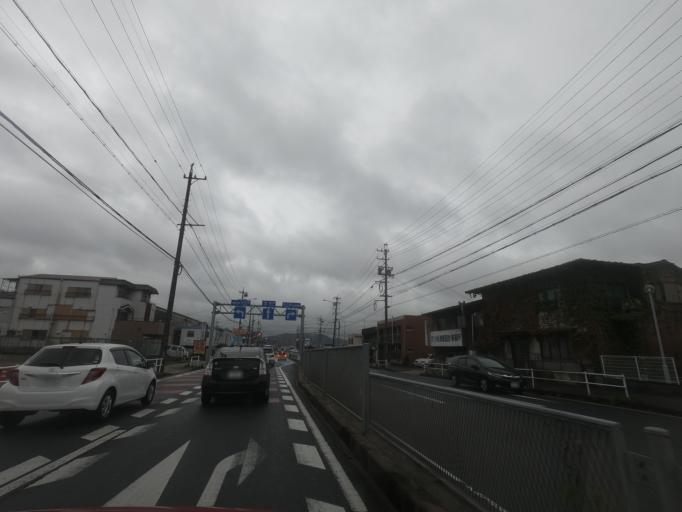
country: JP
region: Aichi
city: Kasugai
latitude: 35.2671
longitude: 137.0129
